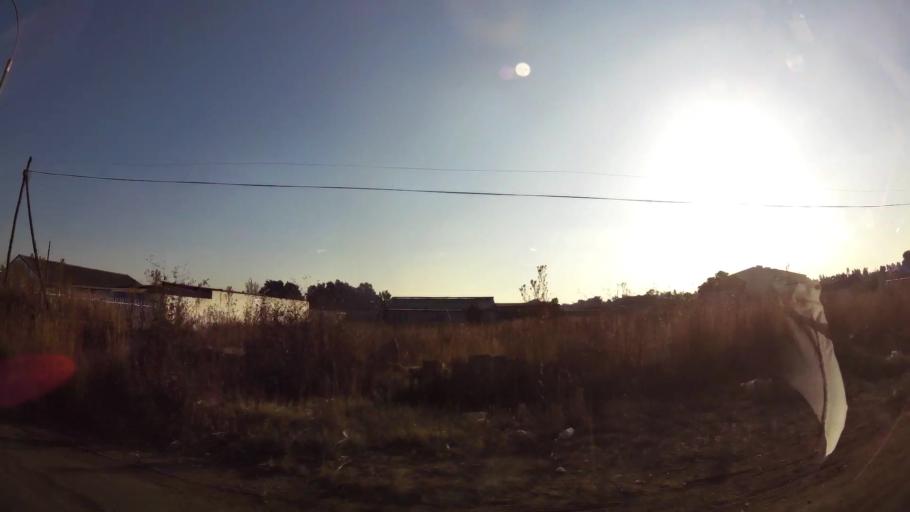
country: ZA
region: Gauteng
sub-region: West Rand District Municipality
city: Randfontein
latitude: -26.1974
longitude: 27.6836
